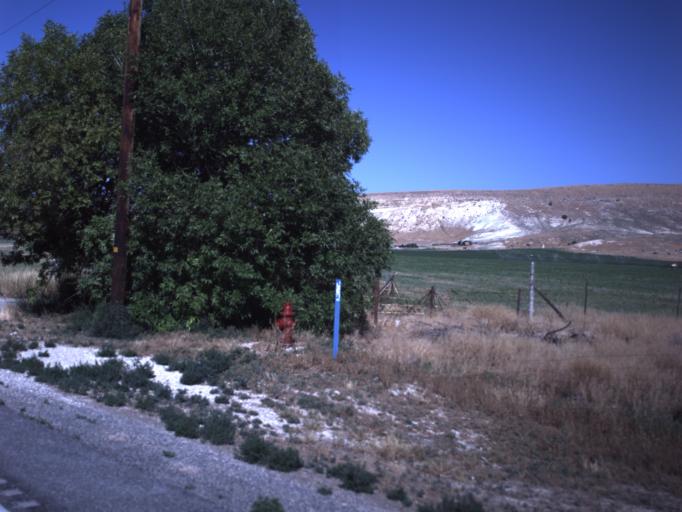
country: US
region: Utah
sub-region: Sanpete County
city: Gunnison
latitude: 39.1583
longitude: -111.7578
